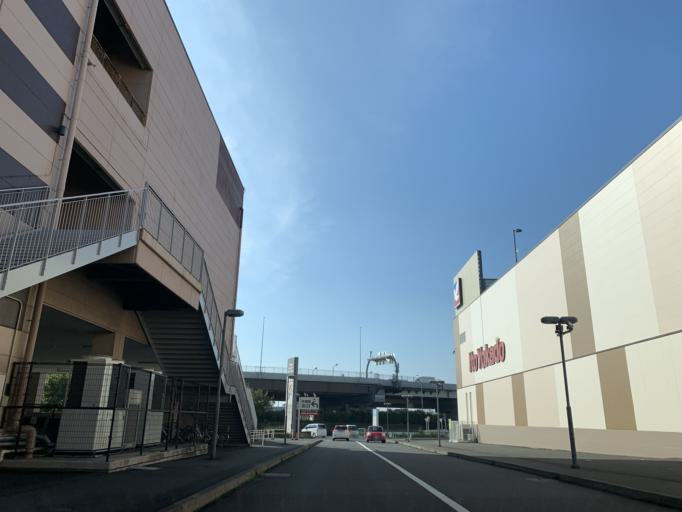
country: JP
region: Saitama
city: Yashio-shi
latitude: 35.8425
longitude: 139.8547
